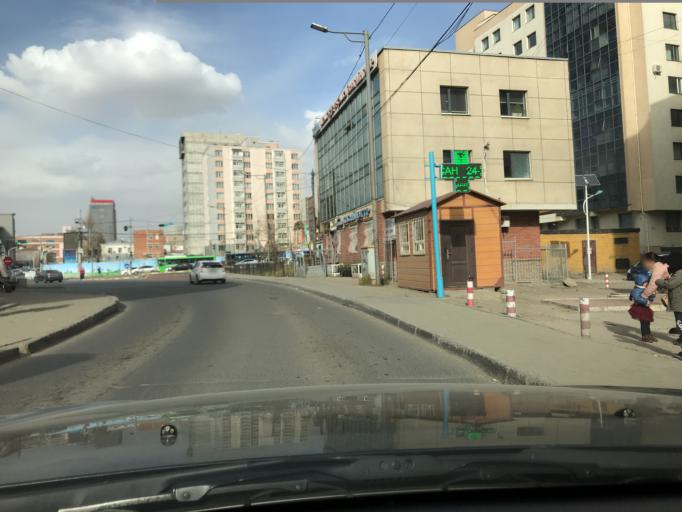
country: MN
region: Ulaanbaatar
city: Ulaanbaatar
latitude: 47.9177
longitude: 106.9358
